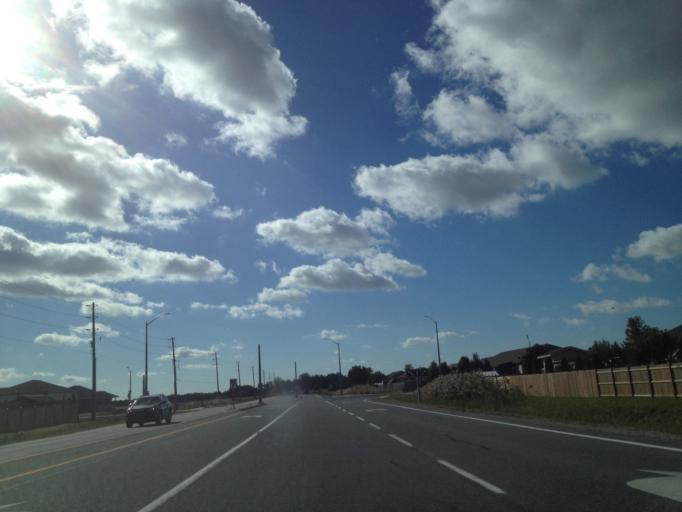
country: CA
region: Ontario
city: Amherstburg
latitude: 42.0409
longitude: -82.5805
